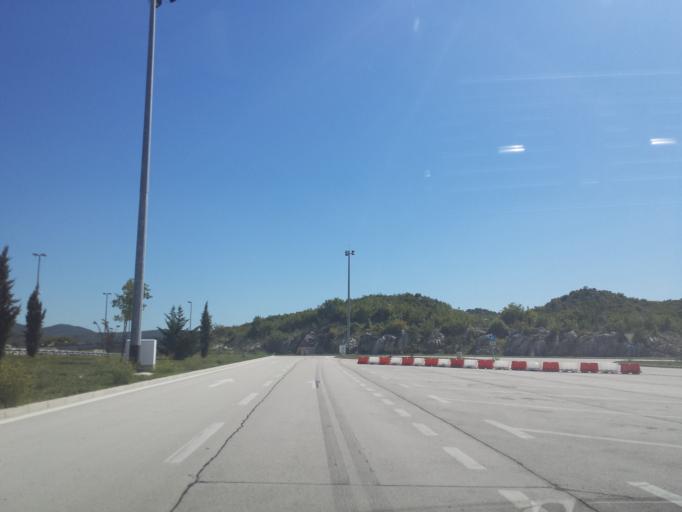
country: HR
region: Splitsko-Dalmatinska
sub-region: Grad Omis
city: Omis
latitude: 43.4925
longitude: 16.7843
